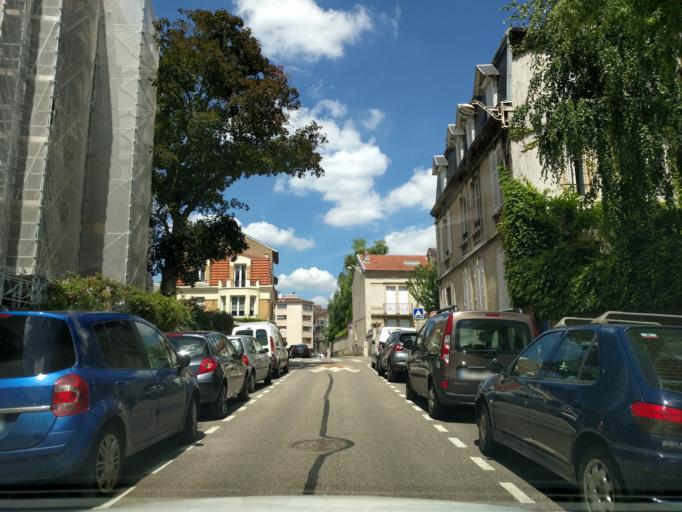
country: FR
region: Lorraine
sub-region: Departement de Meurthe-et-Moselle
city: Laxou
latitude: 48.6853
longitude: 6.1643
